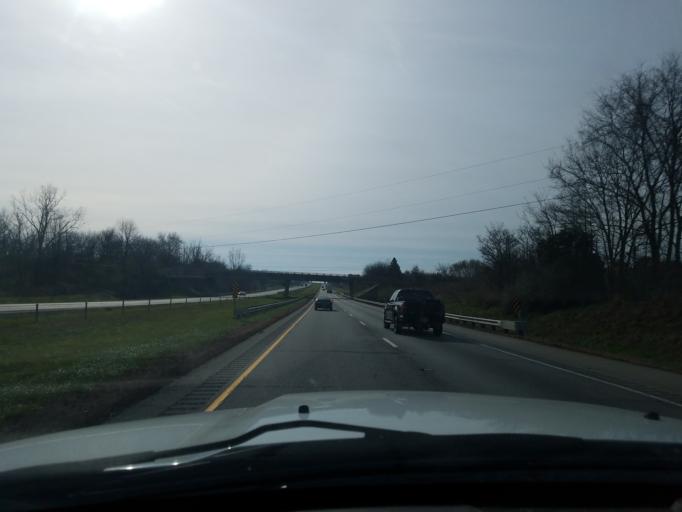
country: US
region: Indiana
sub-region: Madison County
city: Chesterfield
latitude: 40.0785
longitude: -85.5806
